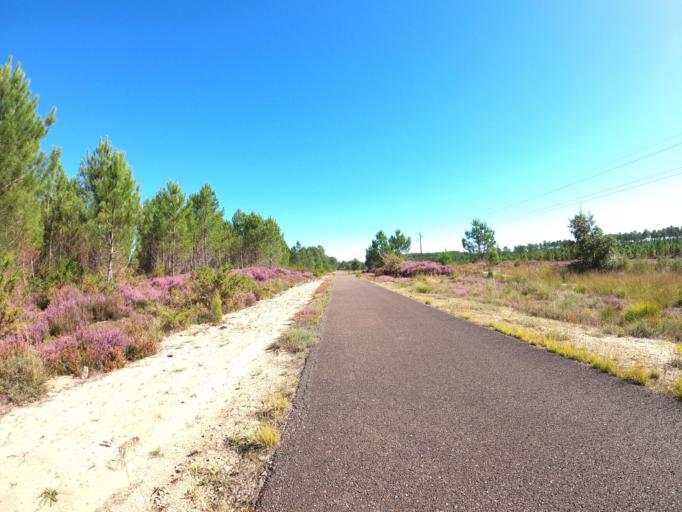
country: FR
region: Aquitaine
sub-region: Departement des Landes
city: Ychoux
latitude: 44.3381
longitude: -0.9571
